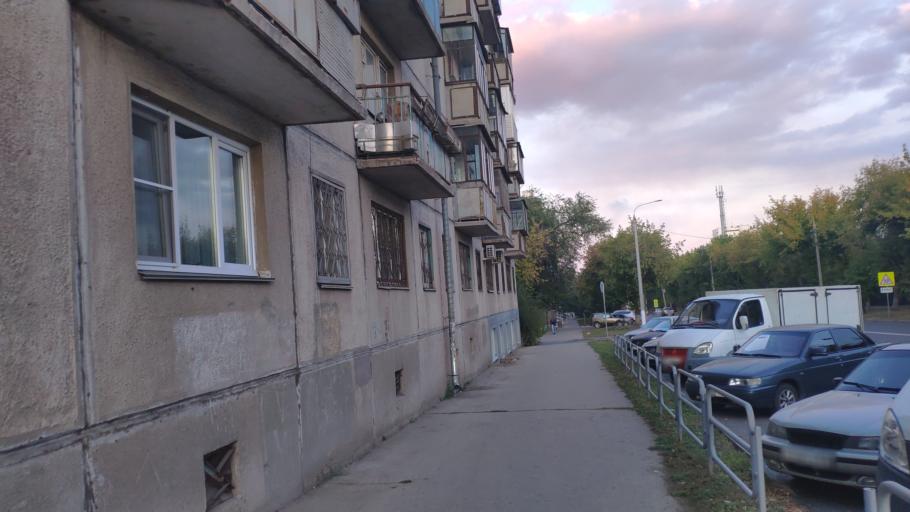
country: RU
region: Chelyabinsk
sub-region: Gorod Magnitogorsk
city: Magnitogorsk
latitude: 53.4118
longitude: 58.9730
